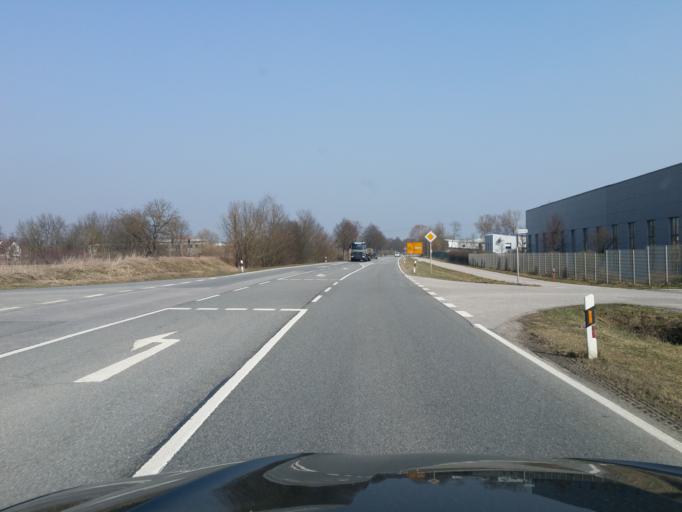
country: DE
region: Bavaria
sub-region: Lower Bavaria
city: Ergolding
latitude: 48.5833
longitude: 12.1991
